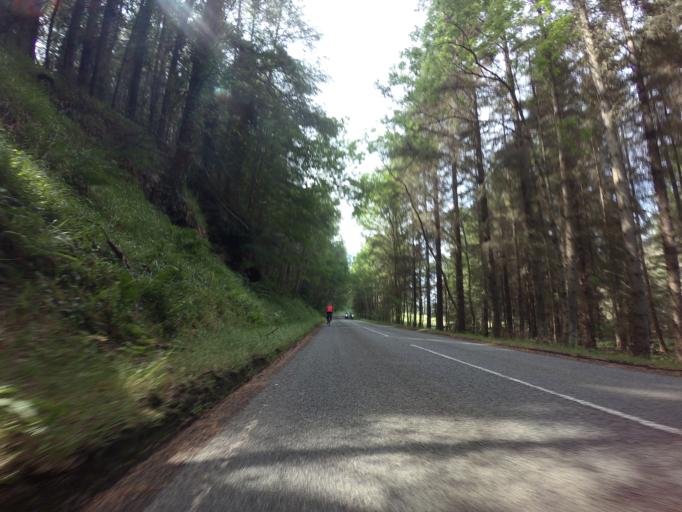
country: GB
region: Scotland
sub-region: Highland
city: Tain
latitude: 57.8269
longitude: -4.1391
